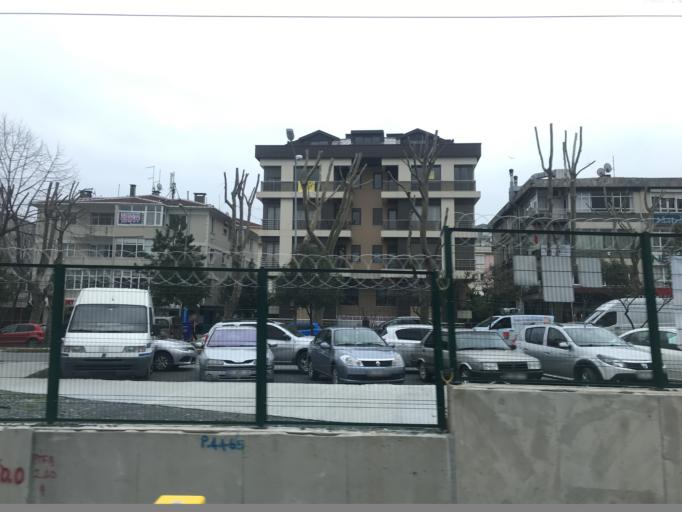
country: TR
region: Istanbul
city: Bahcelievler
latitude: 40.9643
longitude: 28.8362
